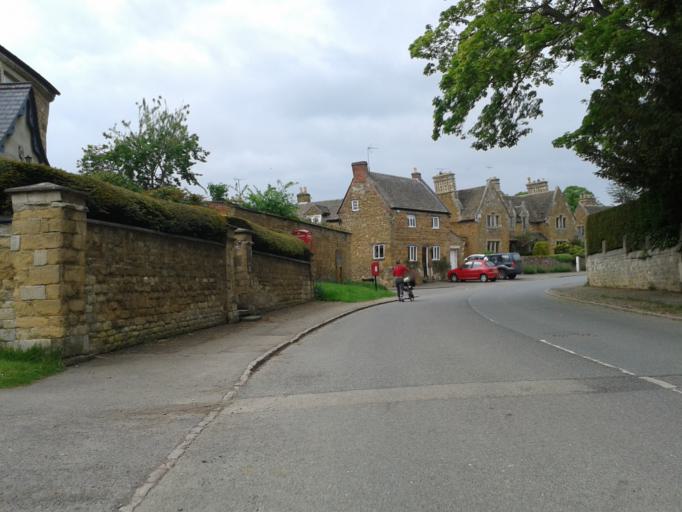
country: GB
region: England
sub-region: Northamptonshire
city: Desborough
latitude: 52.5101
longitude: -0.8303
